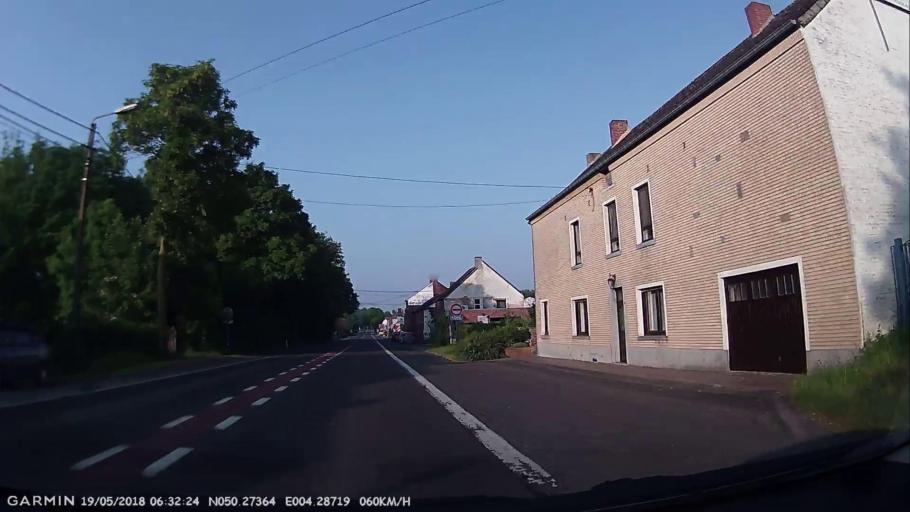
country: BE
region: Wallonia
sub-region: Province du Hainaut
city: Beaumont
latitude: 50.2736
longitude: 4.2871
